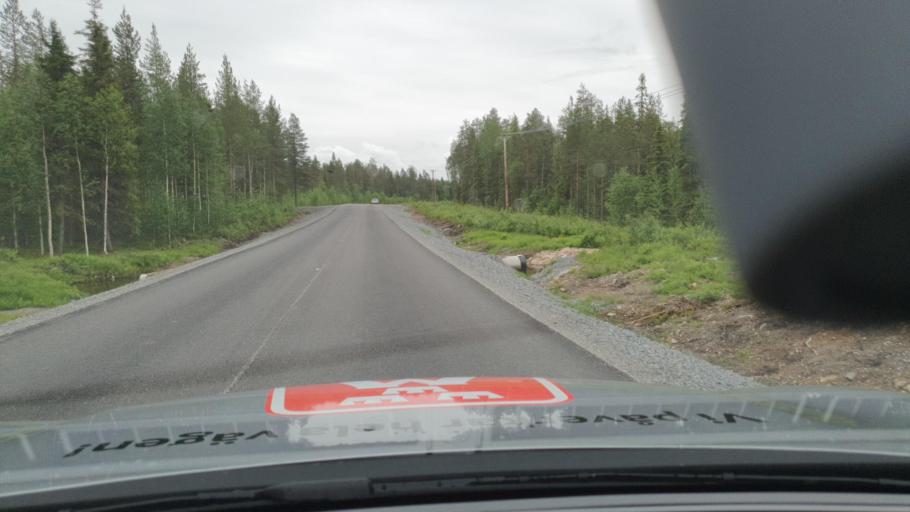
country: SE
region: Norrbotten
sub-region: Overtornea Kommun
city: OEvertornea
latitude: 66.6374
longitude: 23.2584
